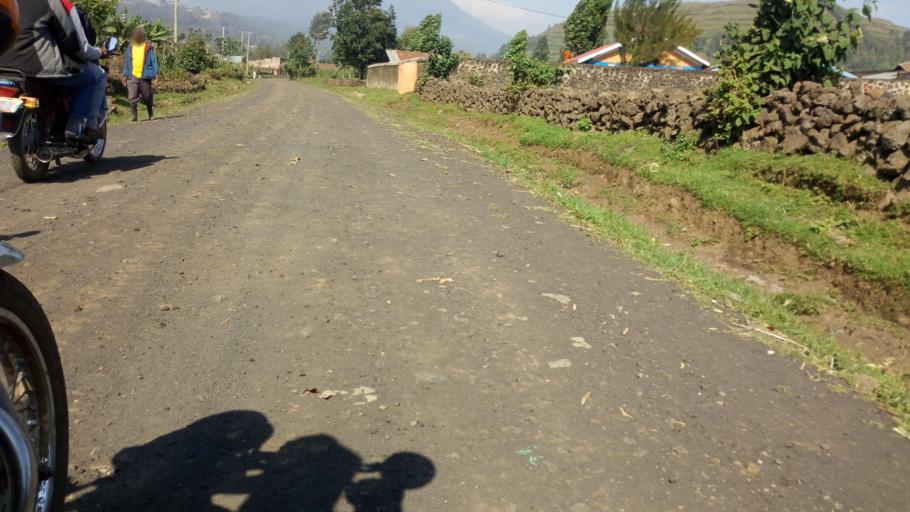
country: UG
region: Western Region
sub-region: Kisoro District
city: Kisoro
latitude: -1.3305
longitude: 29.6402
